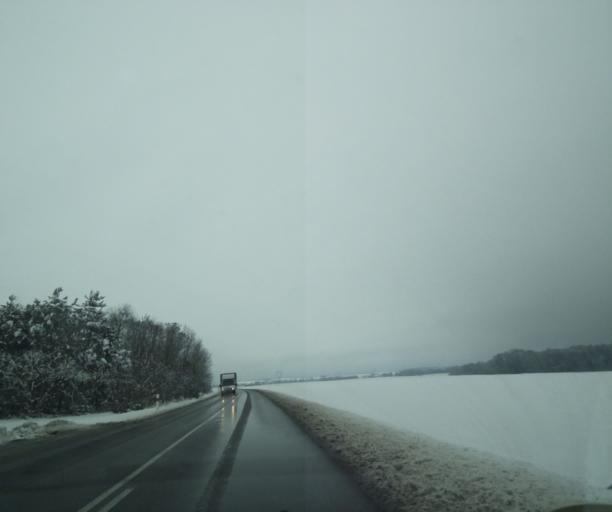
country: FR
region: Champagne-Ardenne
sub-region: Departement de la Haute-Marne
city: Montier-en-Der
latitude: 48.4932
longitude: 4.7802
